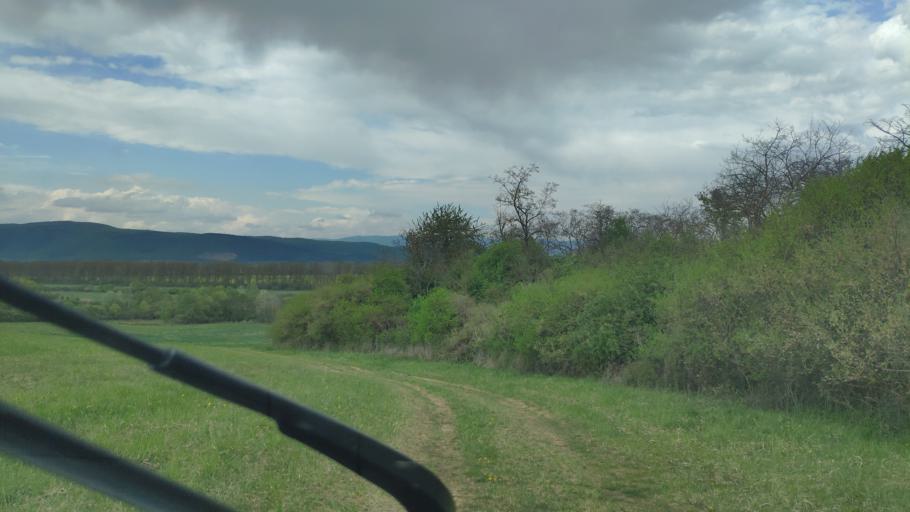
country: SK
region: Kosicky
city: Moldava nad Bodvou
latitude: 48.5571
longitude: 20.9551
